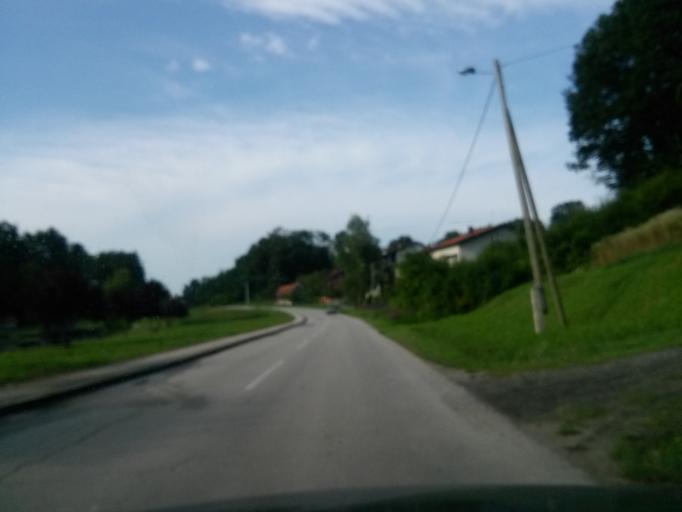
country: HR
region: Sisacko-Moslavacka
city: Gvozd
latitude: 45.2992
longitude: 15.9682
